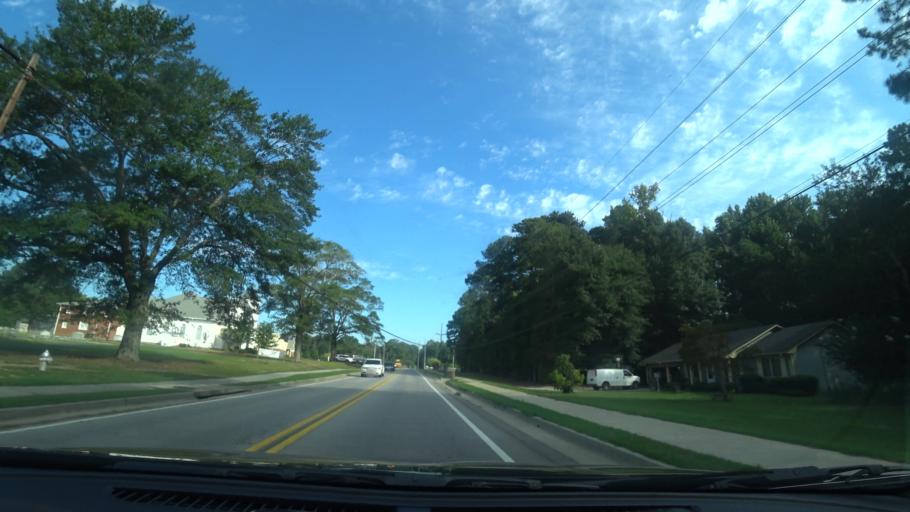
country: US
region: Georgia
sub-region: Gwinnett County
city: Grayson
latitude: 33.8854
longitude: -83.9589
